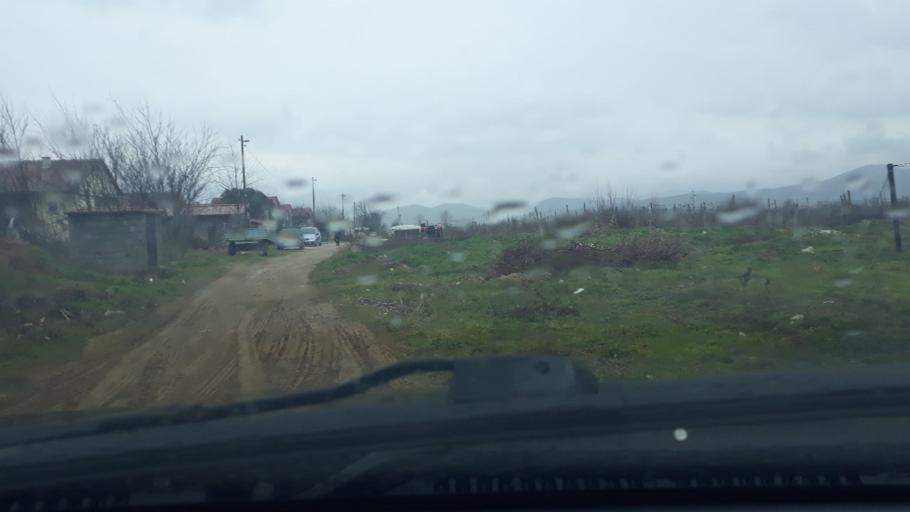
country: MK
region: Valandovo
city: Pirava
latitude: 41.3323
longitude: 22.4822
